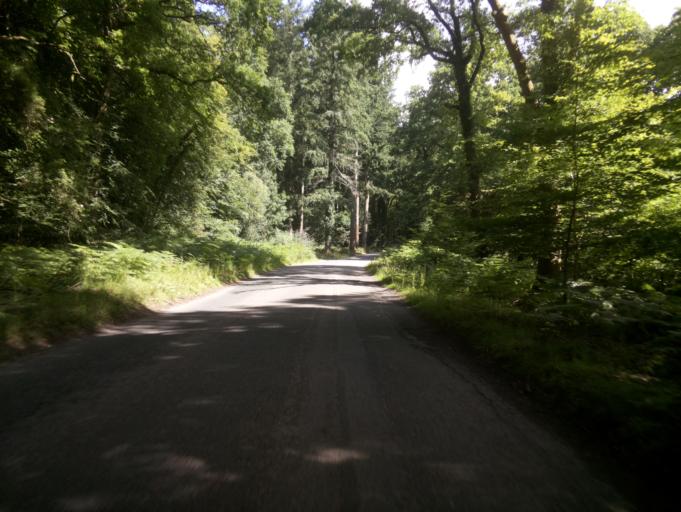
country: GB
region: England
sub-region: Gloucestershire
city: Cinderford
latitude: 51.7816
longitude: -2.4999
